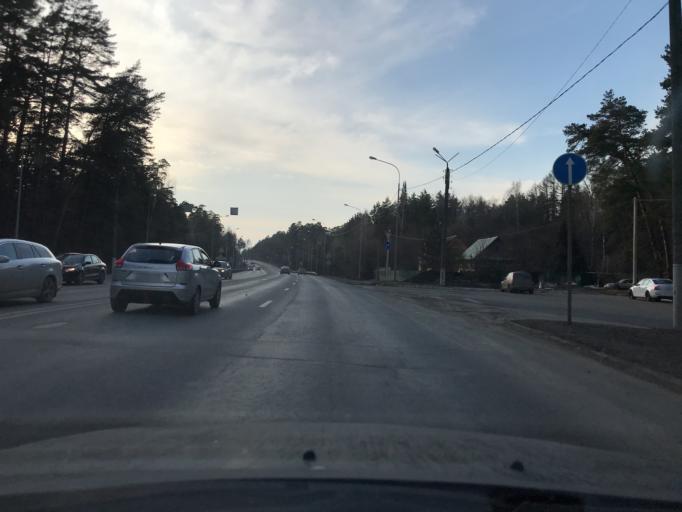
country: RU
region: Kaluga
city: Mstikhino
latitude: 54.5209
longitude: 36.1962
